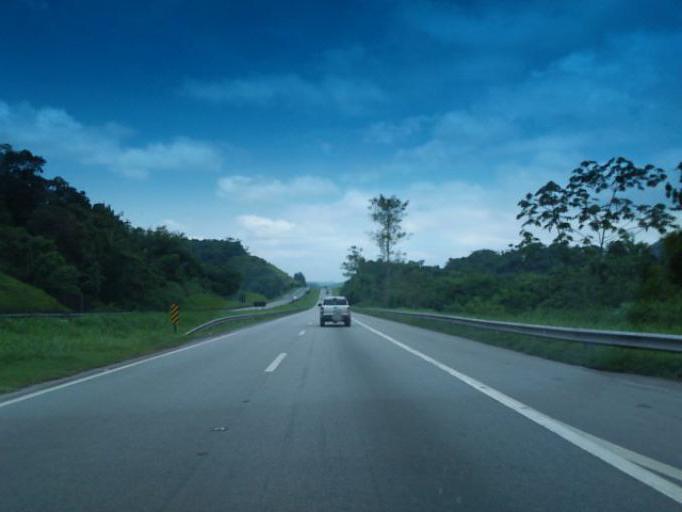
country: BR
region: Sao Paulo
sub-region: Miracatu
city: Miracatu
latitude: -24.1645
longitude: -47.3320
